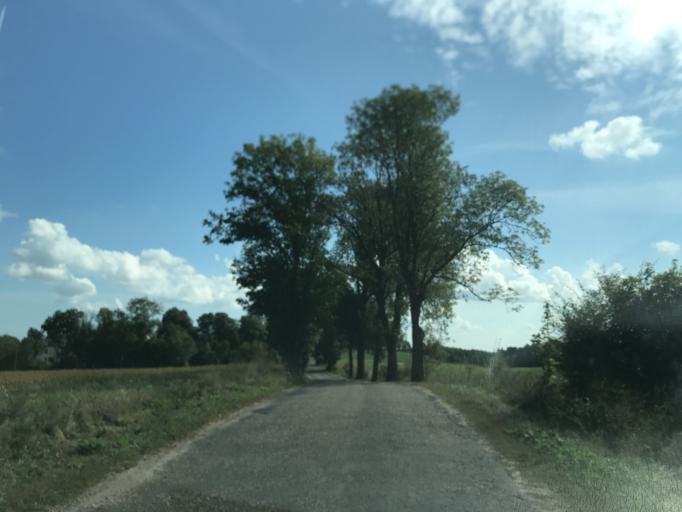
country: PL
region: Kujawsko-Pomorskie
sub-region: Powiat brodnicki
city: Brzozie
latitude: 53.3572
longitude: 19.6177
